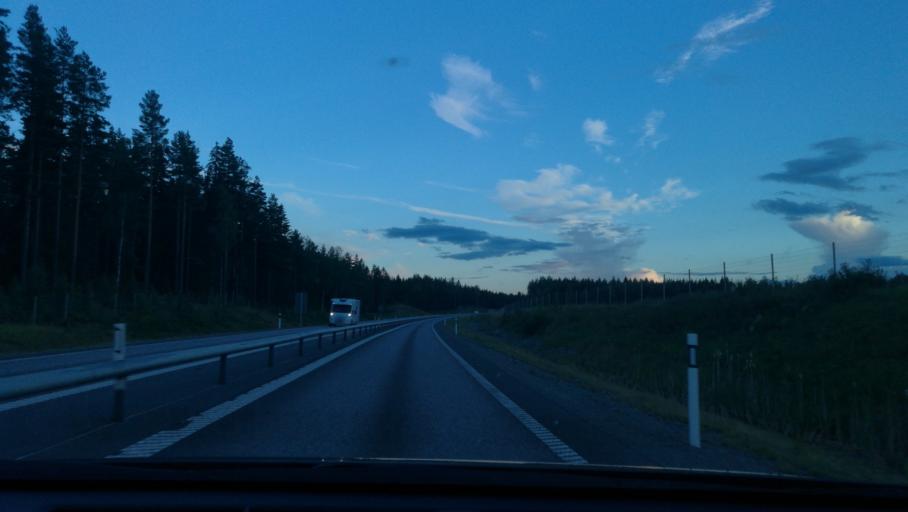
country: SE
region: Soedermanland
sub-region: Katrineholms Kommun
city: Katrineholm
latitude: 58.9837
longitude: 16.2661
